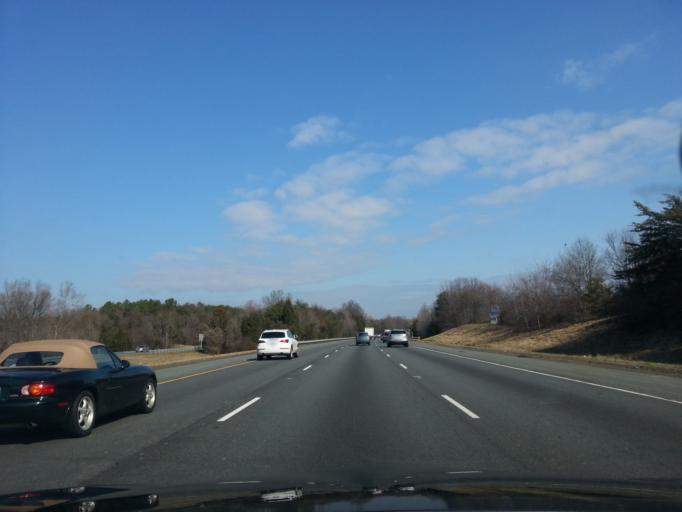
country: US
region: Virginia
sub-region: City of Fredericksburg
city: Fredericksburg
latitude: 38.2562
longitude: -77.5122
